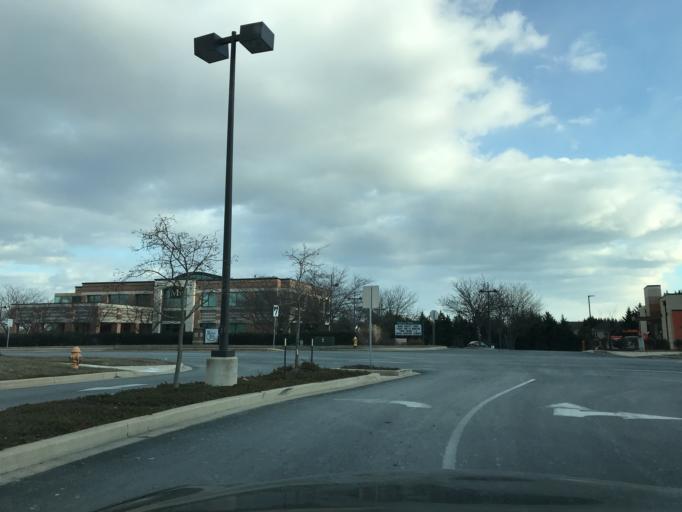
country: US
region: Maryland
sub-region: Harford County
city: Bel Air North
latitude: 39.5702
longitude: -76.3822
